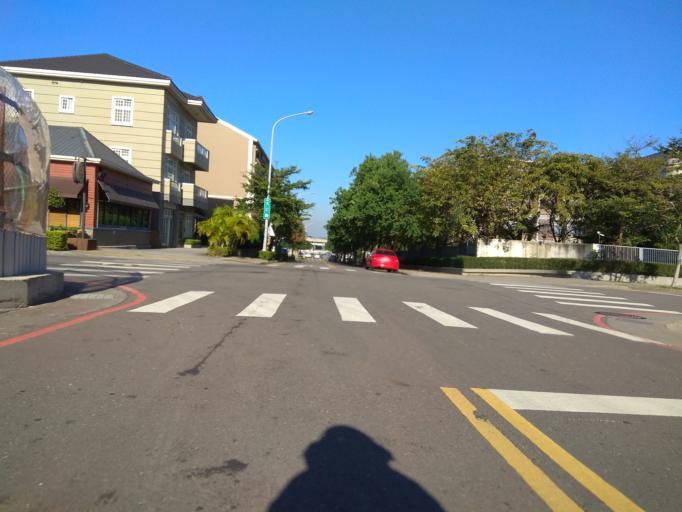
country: TW
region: Taiwan
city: Taoyuan City
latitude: 25.0214
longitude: 121.2194
